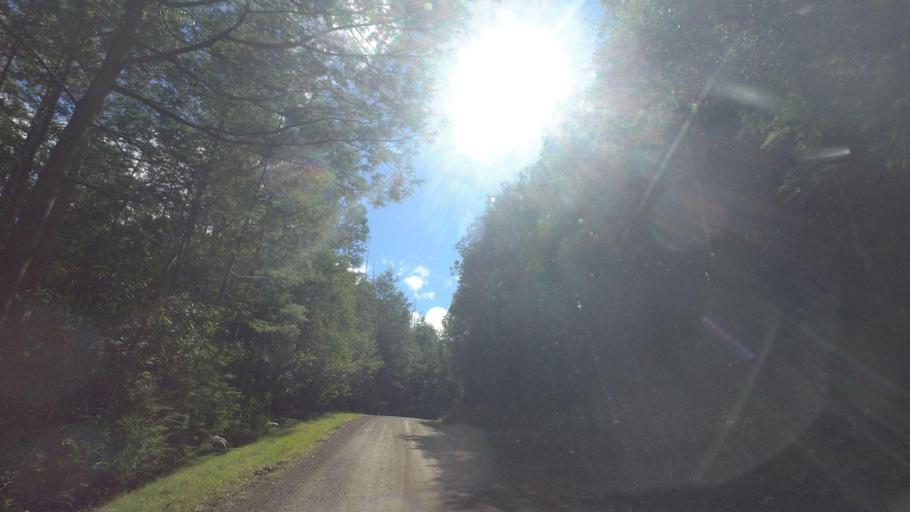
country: AU
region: Victoria
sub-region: Cardinia
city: Bunyip
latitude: -37.9676
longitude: 145.8159
